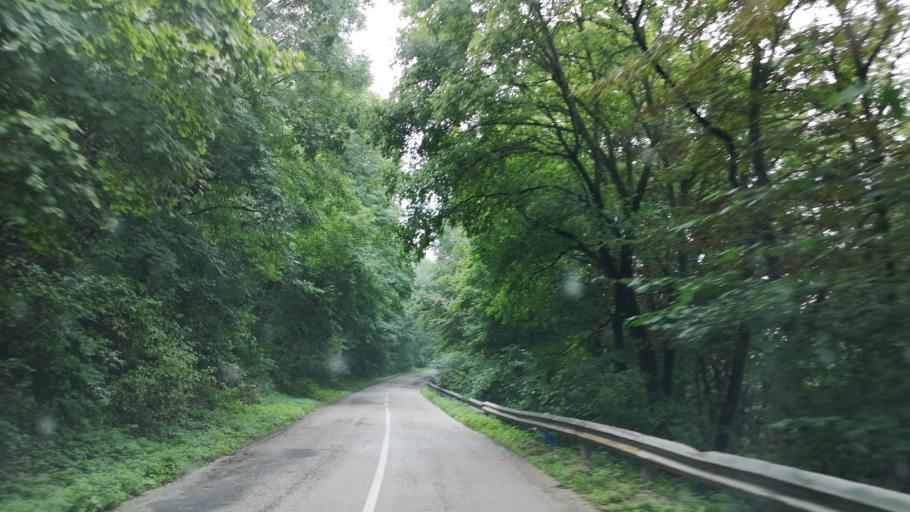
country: SK
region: Trnavsky
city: Smolenice
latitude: 48.5776
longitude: 17.3986
